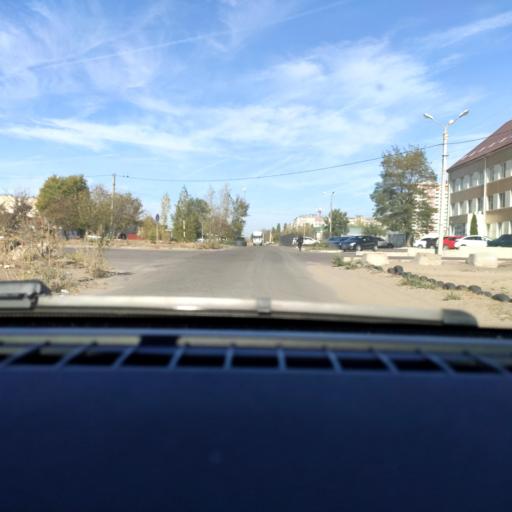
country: RU
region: Voronezj
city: Maslovka
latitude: 51.5908
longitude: 39.2370
